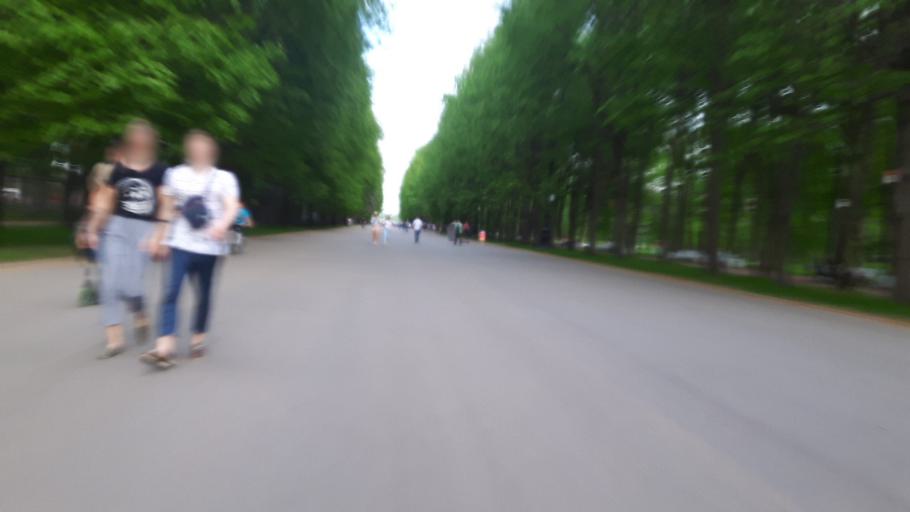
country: RU
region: Leningrad
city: Krestovskiy ostrov
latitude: 59.9717
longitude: 30.2475
